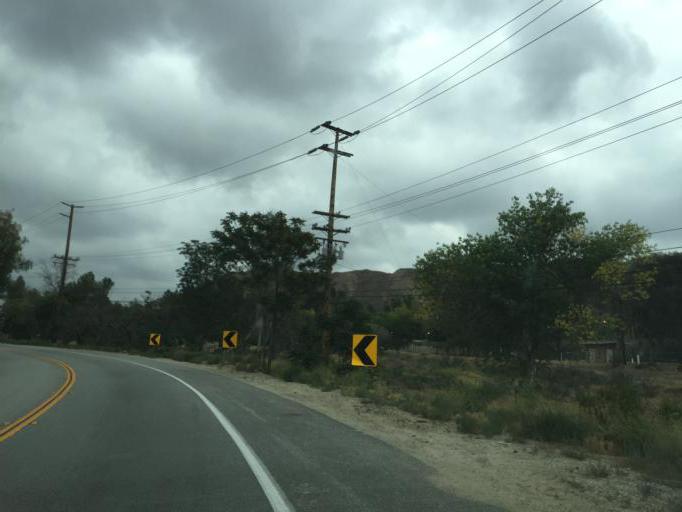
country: US
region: California
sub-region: Los Angeles County
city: Santa Clarita
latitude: 34.4585
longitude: -118.4881
